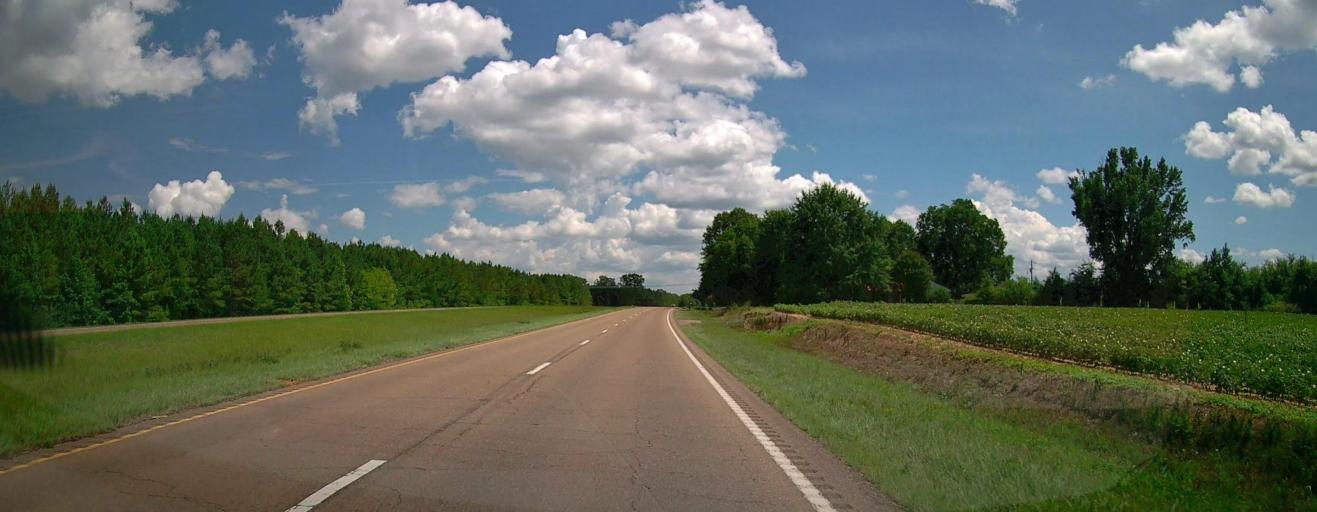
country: US
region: Mississippi
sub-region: Monroe County
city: Aberdeen
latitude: 33.7908
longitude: -88.4602
